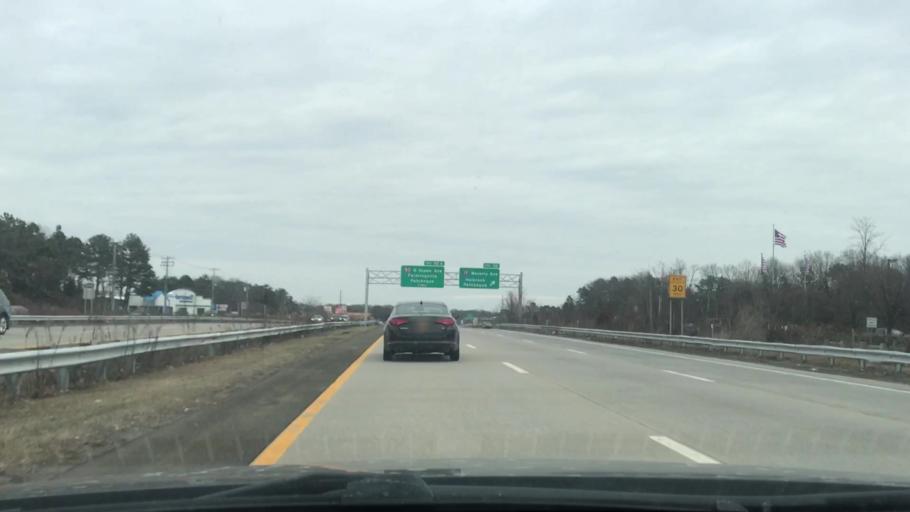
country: US
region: New York
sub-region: Suffolk County
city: Patchogue
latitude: 40.7733
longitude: -73.0435
